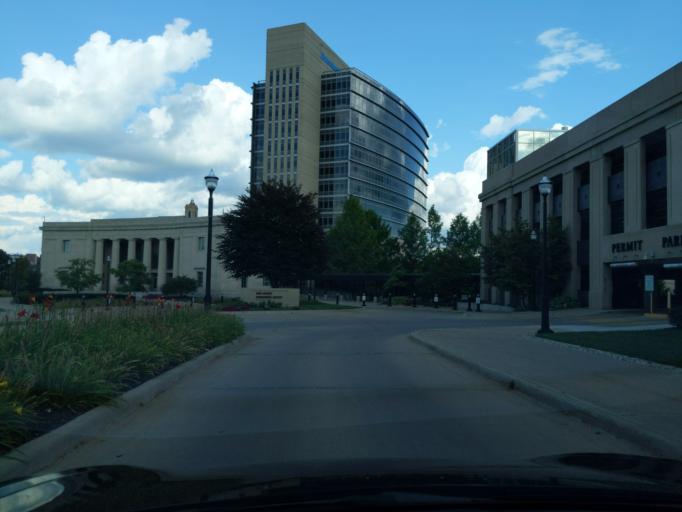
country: US
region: Michigan
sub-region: Jackson County
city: Jackson
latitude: 42.2467
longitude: -84.4038
